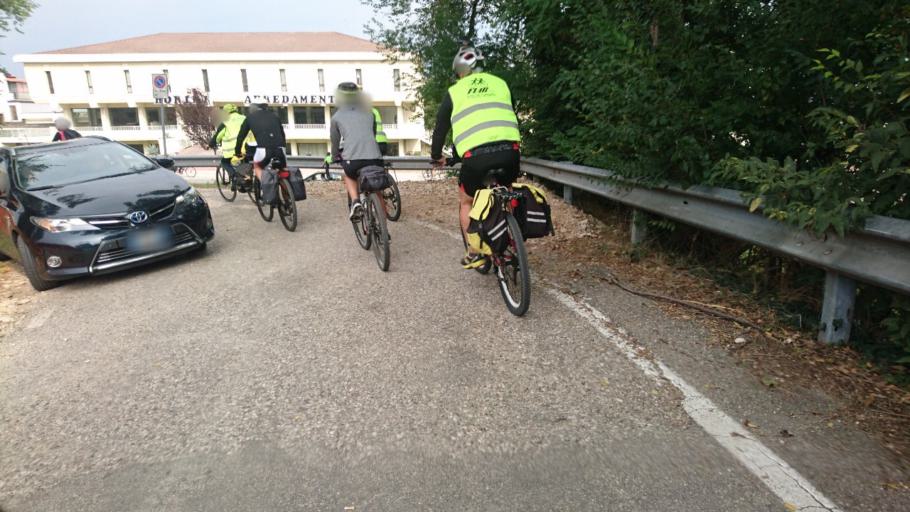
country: IT
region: Veneto
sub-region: Provincia di Verona
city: Caldiero
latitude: 45.4128
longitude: 11.1950
